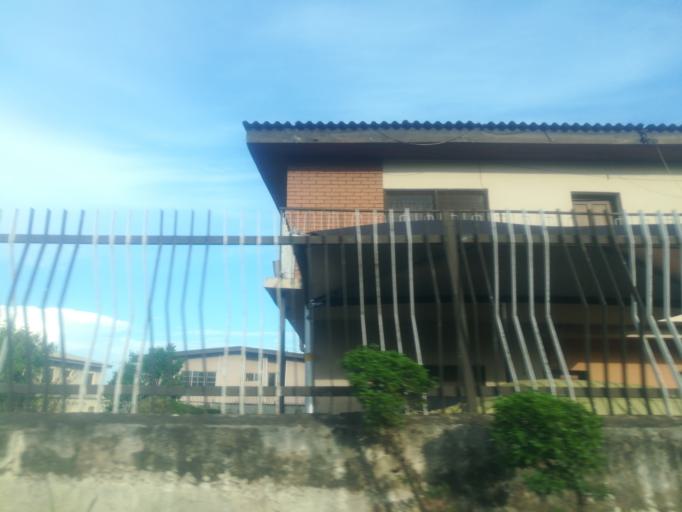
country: NG
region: Oyo
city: Ibadan
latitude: 7.3382
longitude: 3.8902
